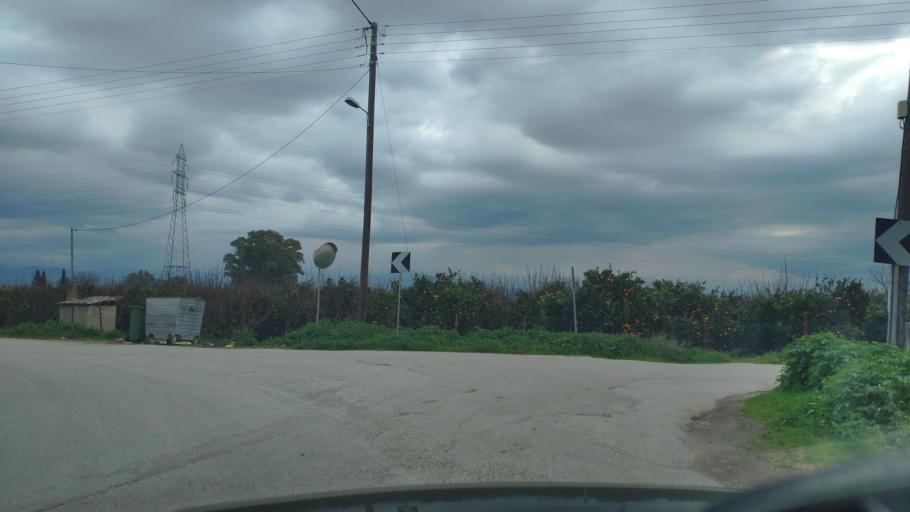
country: GR
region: Peloponnese
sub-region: Nomos Argolidos
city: Nea Kios
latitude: 37.5951
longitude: 22.7018
